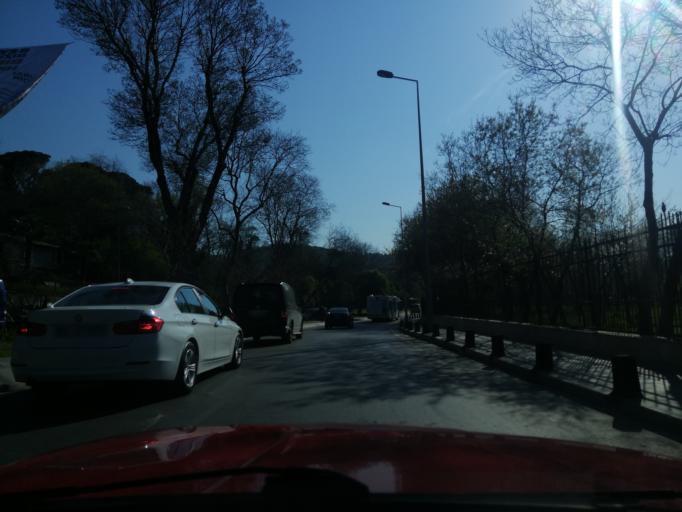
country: TR
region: Istanbul
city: UEskuedar
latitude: 41.0796
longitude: 29.0692
